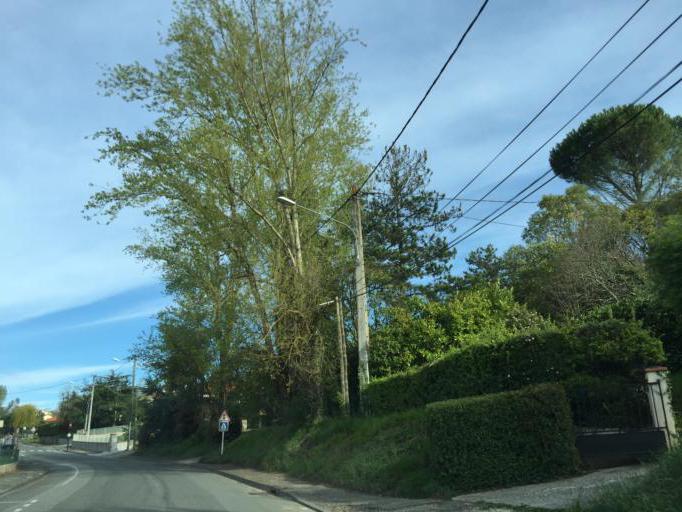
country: FR
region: Midi-Pyrenees
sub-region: Departement de la Haute-Garonne
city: Montastruc-la-Conseillere
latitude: 43.7197
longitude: 1.5937
